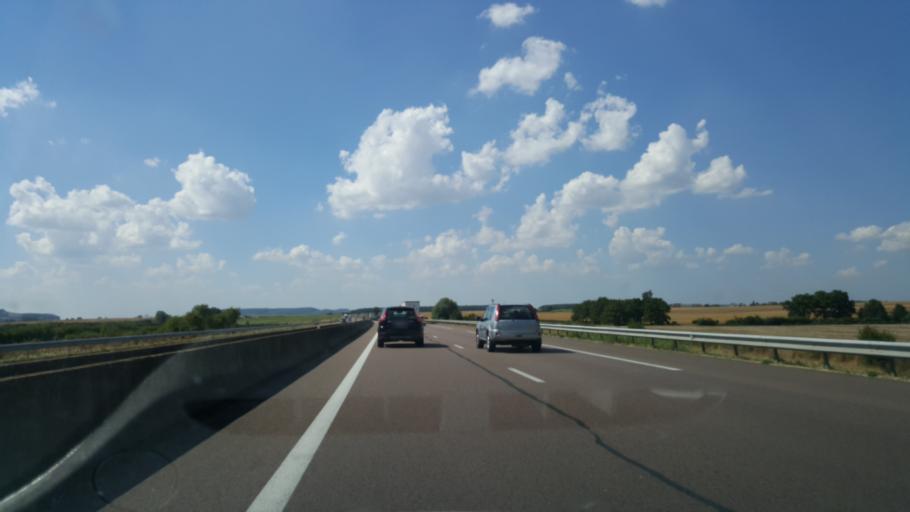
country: FR
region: Bourgogne
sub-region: Departement de la Cote-d'Or
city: Vitteaux
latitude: 47.3524
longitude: 4.4470
